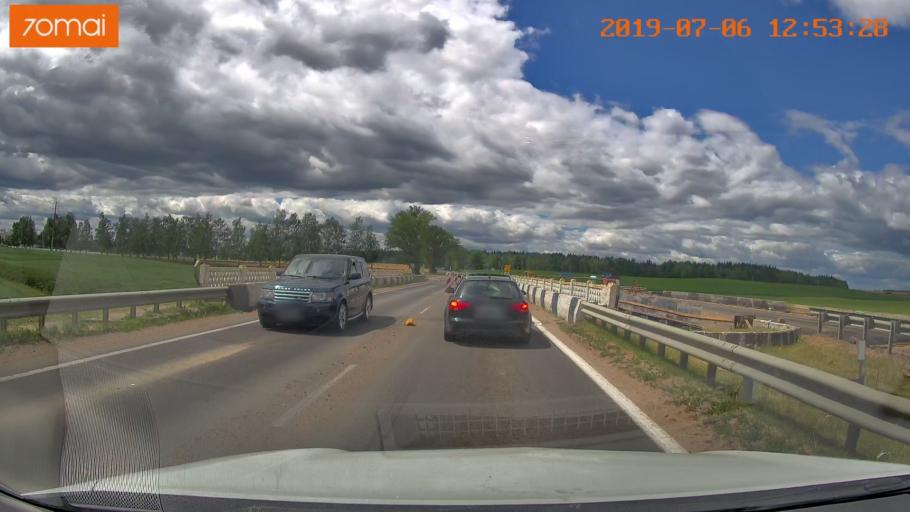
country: BY
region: Minsk
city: Dzyarzhynsk
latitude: 53.7038
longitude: 27.2027
